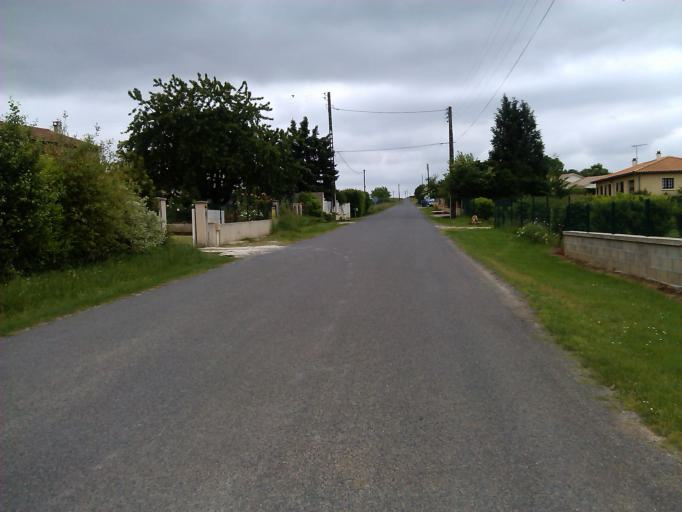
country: FR
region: Poitou-Charentes
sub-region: Departement de la Charente
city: Chateauneuf-sur-Charente
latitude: 45.5855
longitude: -0.0554
